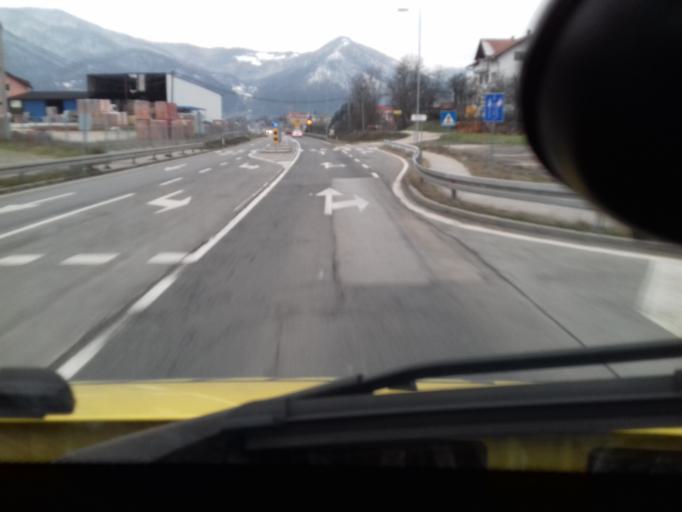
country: BA
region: Federation of Bosnia and Herzegovina
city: Zepce
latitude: 44.4354
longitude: 18.0379
